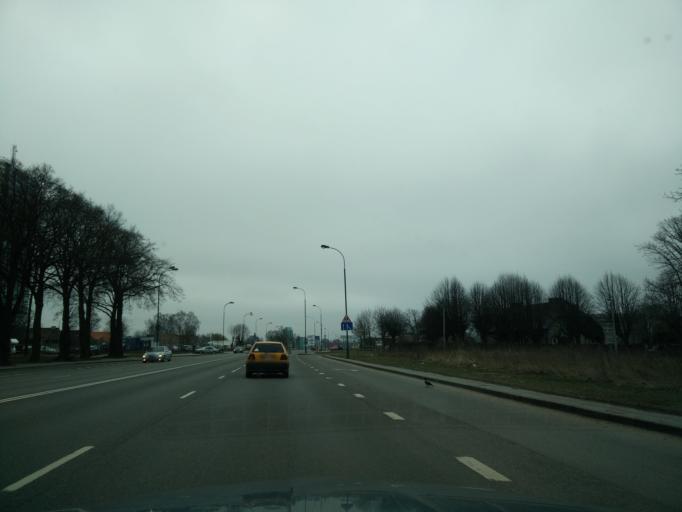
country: LT
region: Klaipedos apskritis
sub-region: Klaipeda
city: Klaipeda
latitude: 55.6931
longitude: 21.1417
